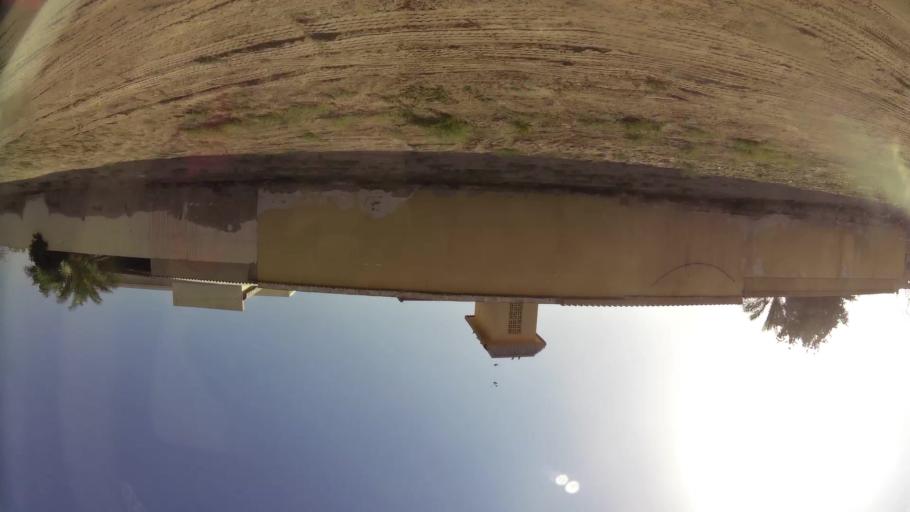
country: AE
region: Ajman
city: Ajman
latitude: 25.4065
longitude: 55.4632
